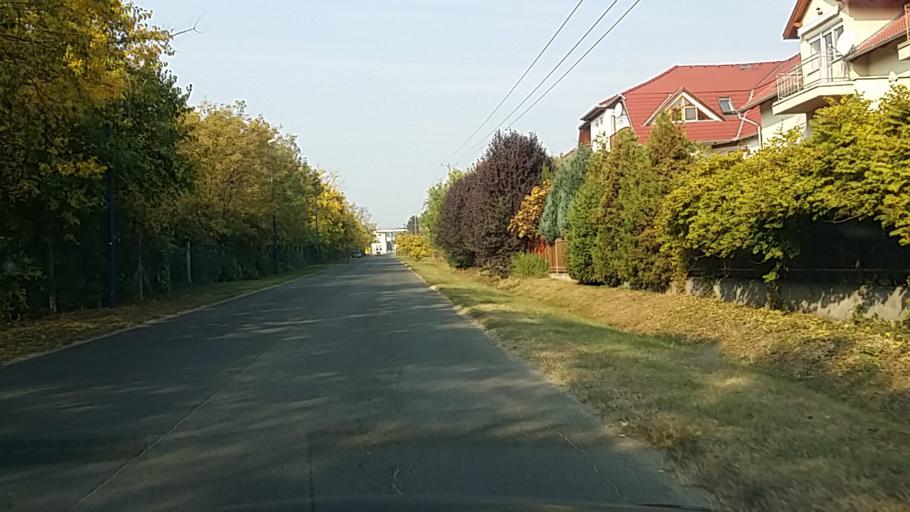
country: HU
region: Pest
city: Dunakeszi
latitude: 47.6163
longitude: 19.1569
